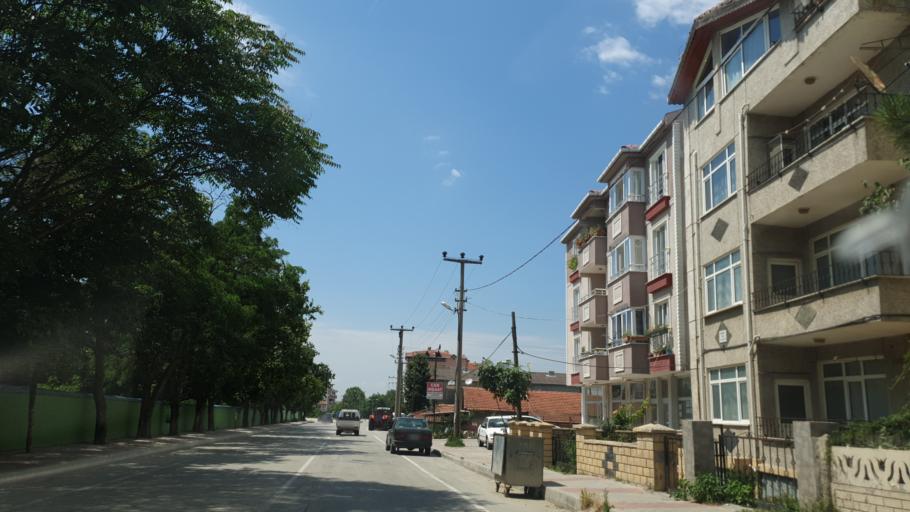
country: TR
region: Tekirdag
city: Saray
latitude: 41.4396
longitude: 27.9154
